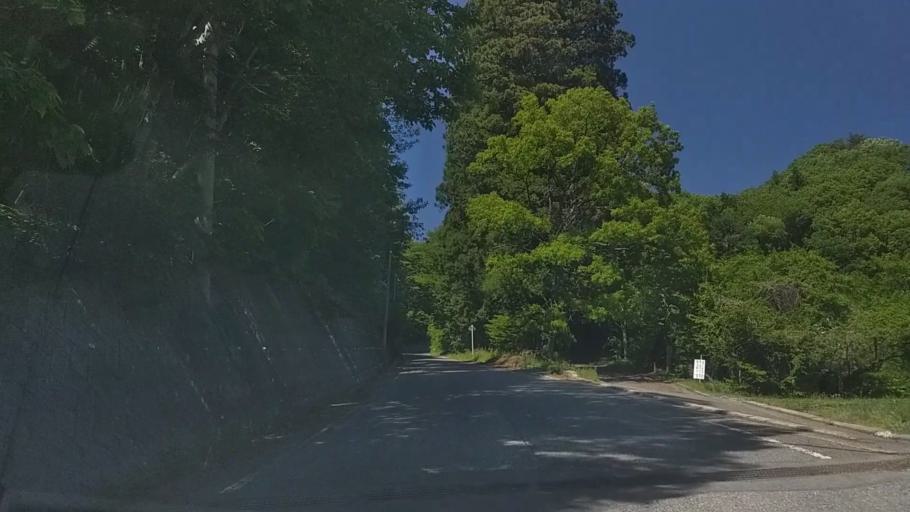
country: JP
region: Yamanashi
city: Nirasaki
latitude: 35.8623
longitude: 138.4471
